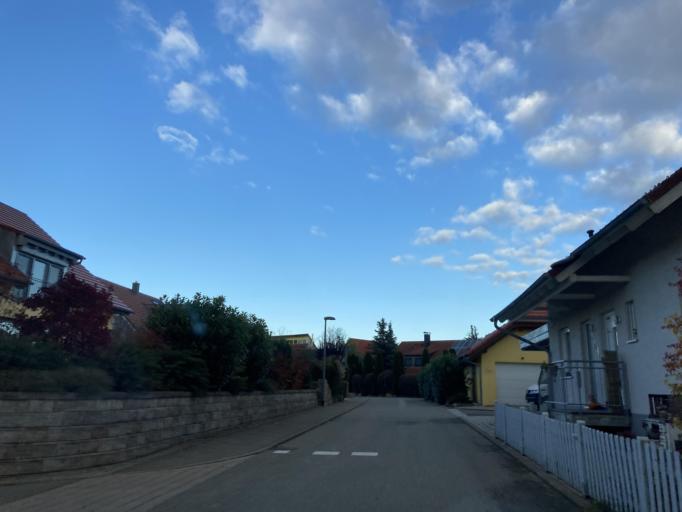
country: DE
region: Baden-Wuerttemberg
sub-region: Tuebingen Region
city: Haigerloch
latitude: 48.4295
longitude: 8.7879
